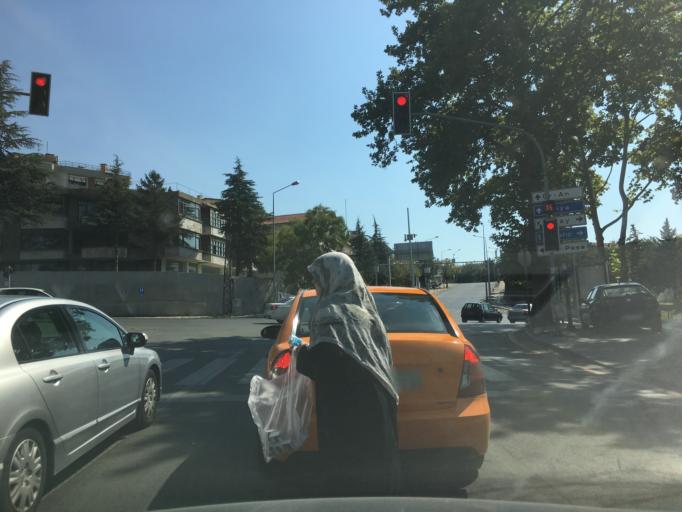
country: TR
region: Ankara
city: Cankaya
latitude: 39.8935
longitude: 32.8686
